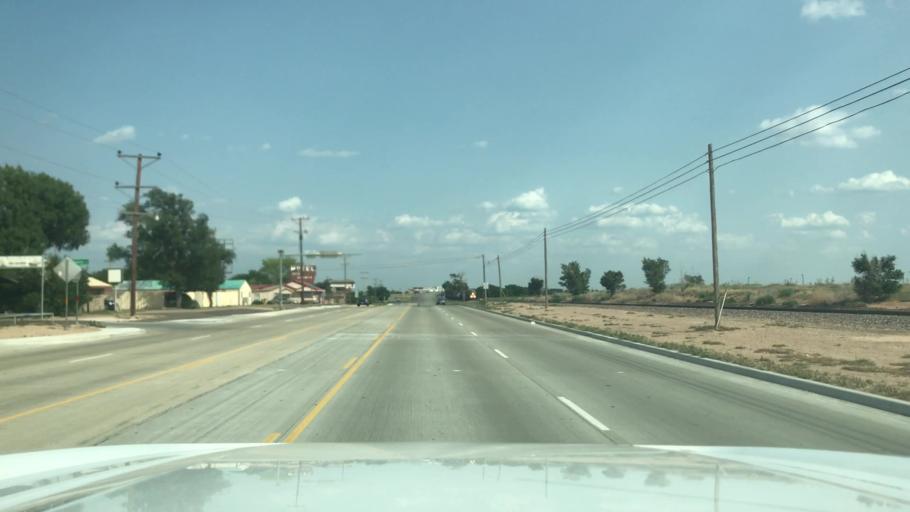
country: US
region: Texas
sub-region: Dallam County
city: Dalhart
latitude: 36.0503
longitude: -102.4997
